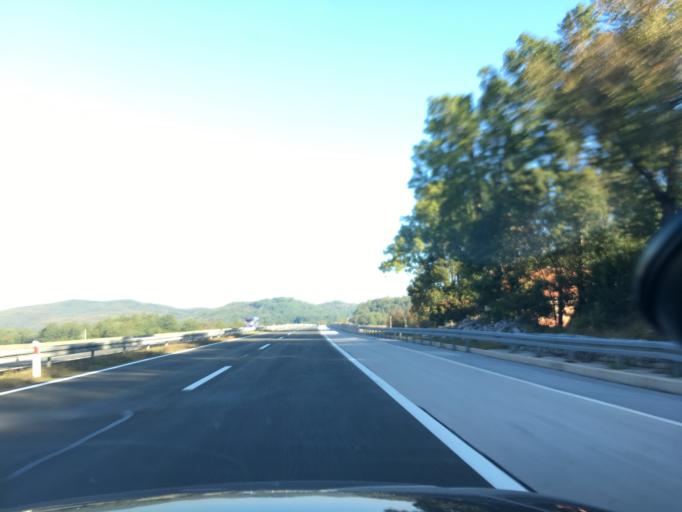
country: HR
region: Zadarska
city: Obrovac
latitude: 44.3448
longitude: 15.6462
